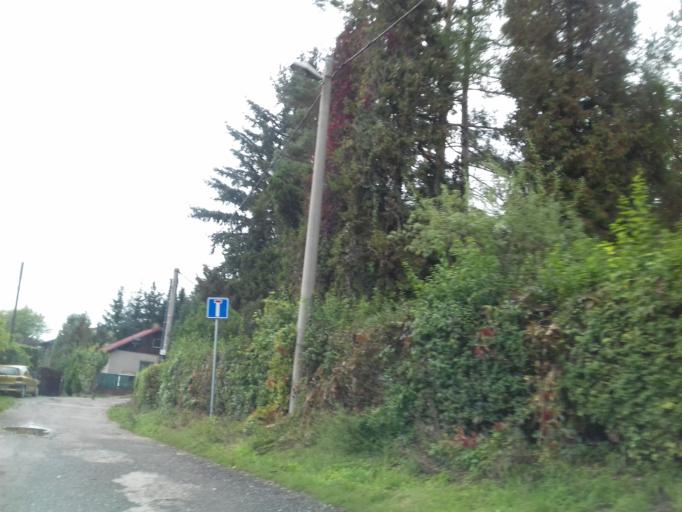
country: CZ
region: Central Bohemia
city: Revnice
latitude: 49.9207
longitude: 14.2306
